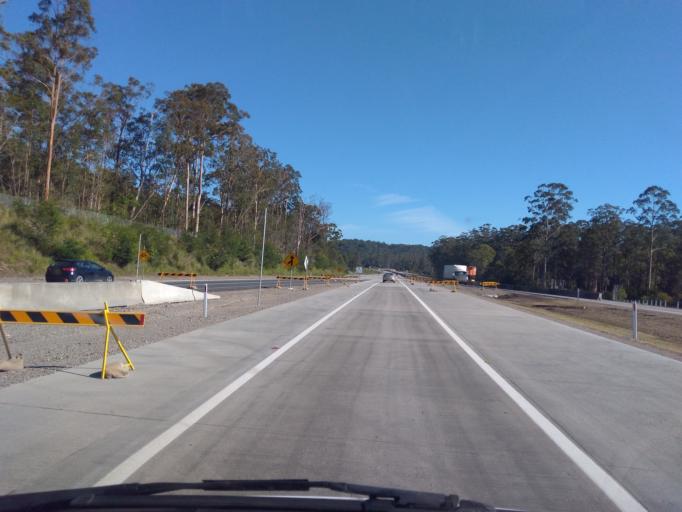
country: AU
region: New South Wales
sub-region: Port Macquarie-Hastings
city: North Shore
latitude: -31.3024
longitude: 152.8219
